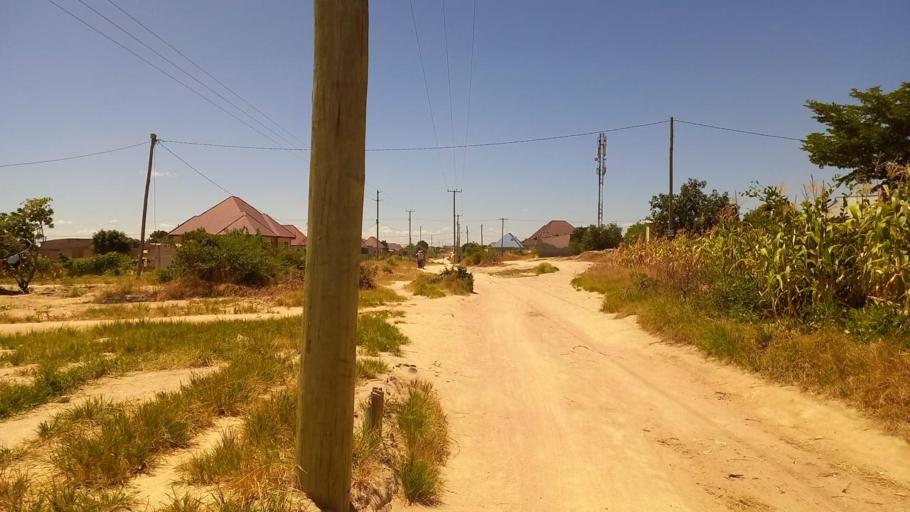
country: TZ
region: Dodoma
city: Dodoma
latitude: -6.1332
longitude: 35.7178
